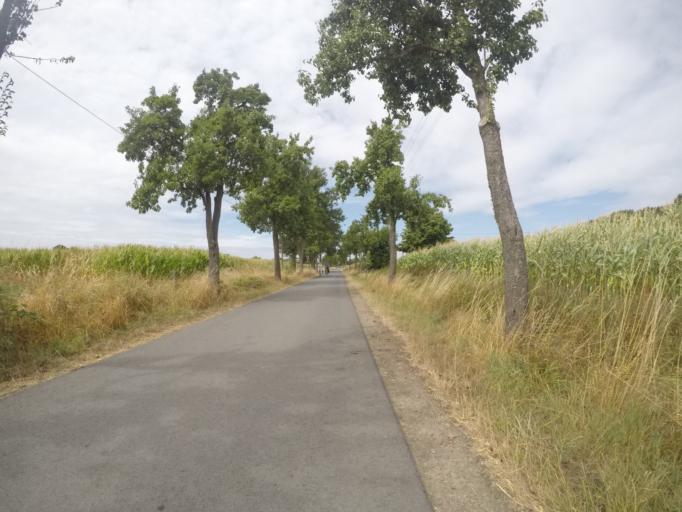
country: DE
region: North Rhine-Westphalia
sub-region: Regierungsbezirk Dusseldorf
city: Bocholt
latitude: 51.8540
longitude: 6.5620
